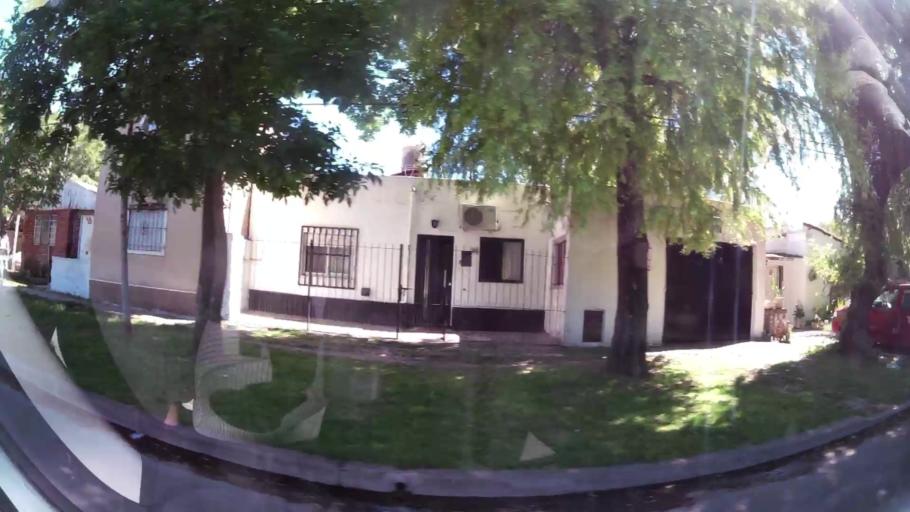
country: AR
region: Buenos Aires
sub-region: Partido de Tigre
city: Tigre
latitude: -34.5042
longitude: -58.6139
